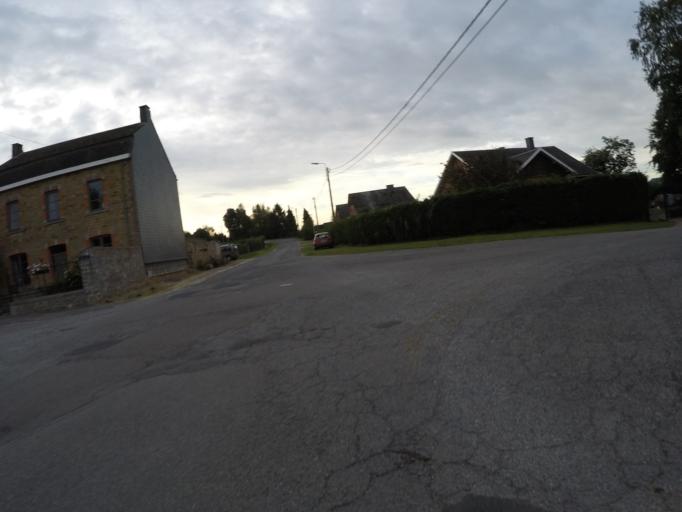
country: BE
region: Wallonia
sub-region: Province de Namur
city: Assesse
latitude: 50.3342
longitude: 5.0618
